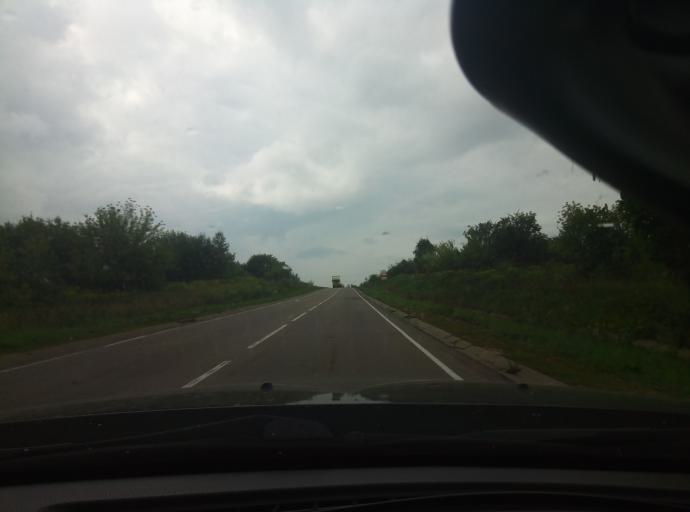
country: RU
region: Tula
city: Lomintsevskiy
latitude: 53.9421
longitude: 37.6330
